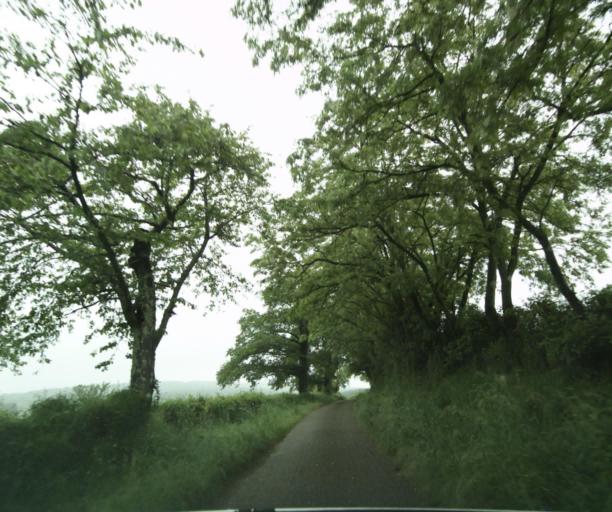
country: FR
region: Bourgogne
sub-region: Departement de Saone-et-Loire
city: Charolles
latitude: 46.4505
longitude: 4.3977
